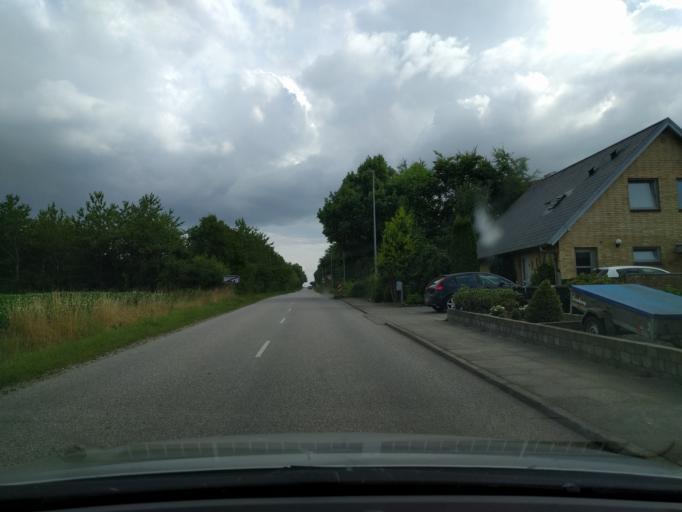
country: DK
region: Central Jutland
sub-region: Herning Kommune
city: Snejbjerg
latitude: 56.1304
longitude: 8.9060
